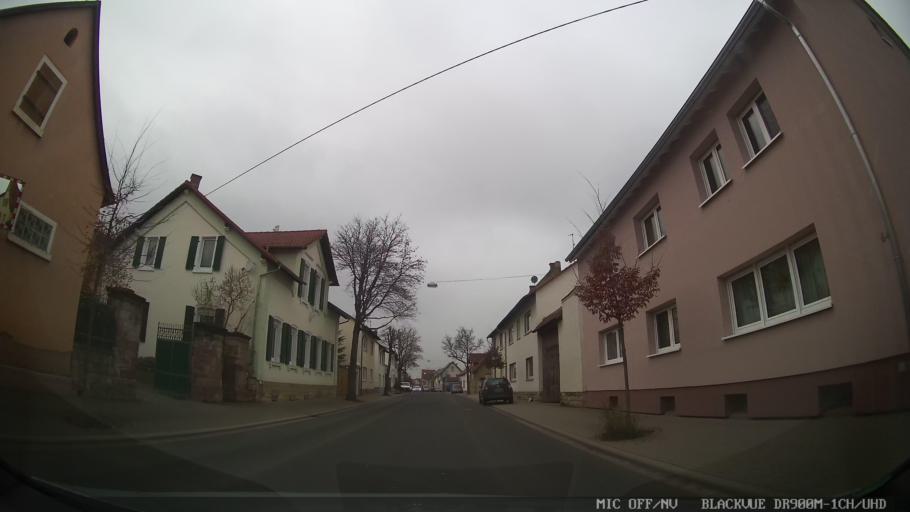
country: DE
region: Rheinland-Pfalz
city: Gau-Odernheim
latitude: 49.7810
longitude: 8.1973
